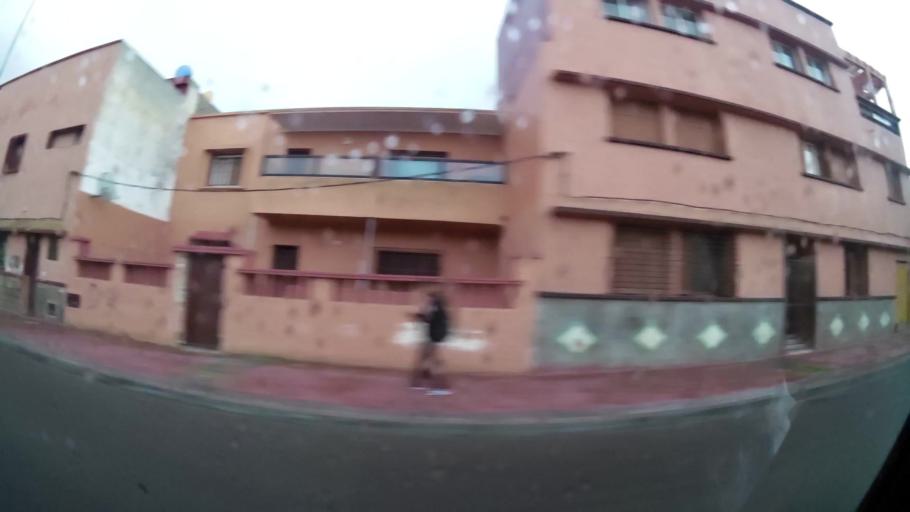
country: MA
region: Doukkala-Abda
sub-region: El-Jadida
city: El Jadida
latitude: 33.2592
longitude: -8.5095
